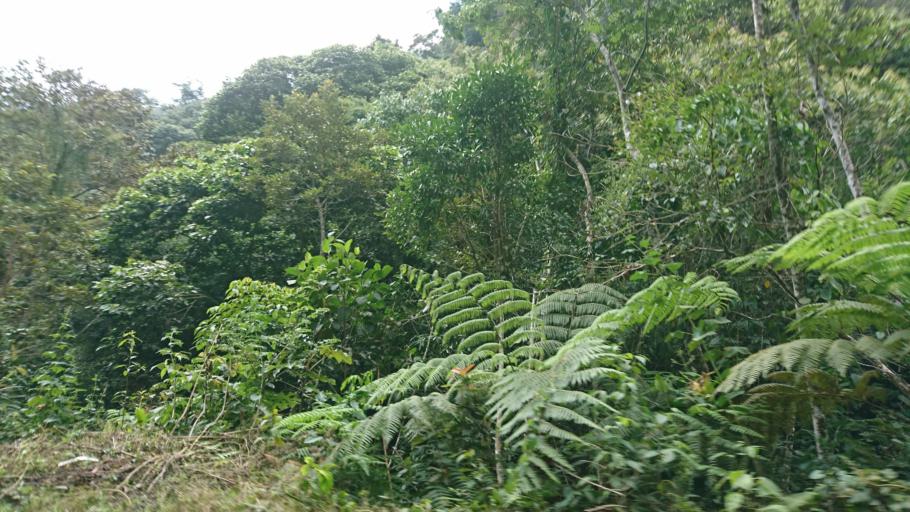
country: BO
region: La Paz
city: Coroico
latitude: -16.1155
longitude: -67.7839
